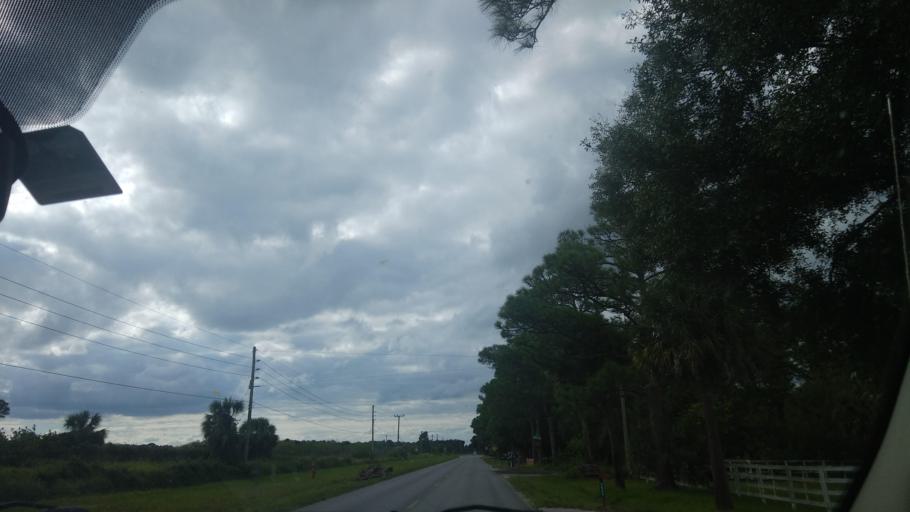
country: US
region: Florida
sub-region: Saint Lucie County
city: Lakewood Park
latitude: 27.5208
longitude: -80.3754
